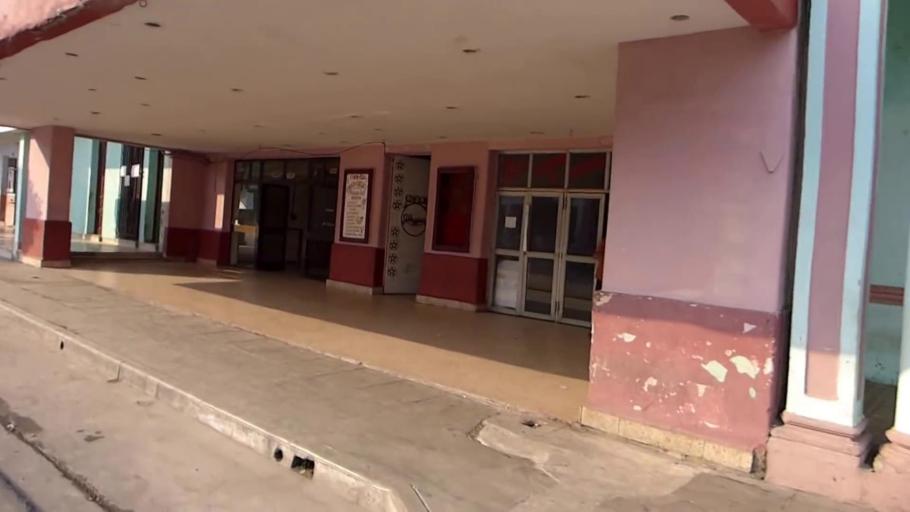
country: CU
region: Camaguey
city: Camaguey
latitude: 21.3745
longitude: -77.9129
